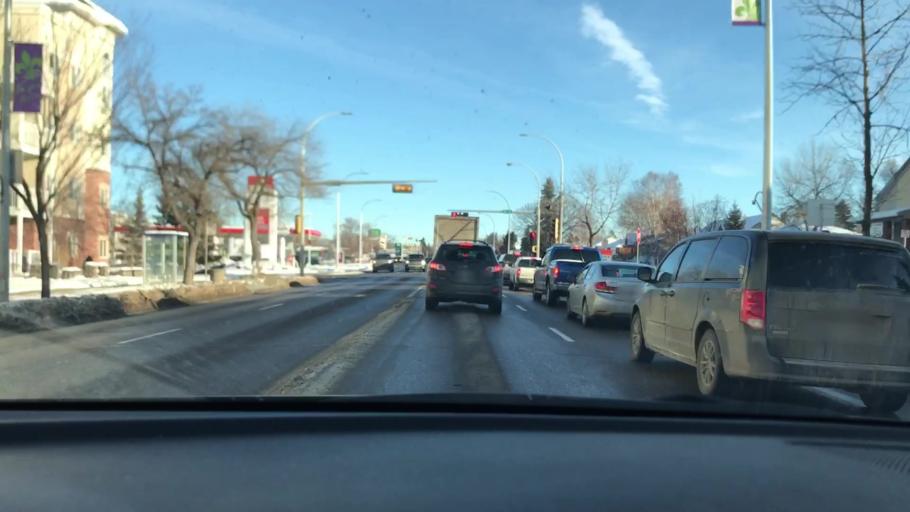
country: CA
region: Alberta
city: Edmonton
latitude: 53.5180
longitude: -113.4594
